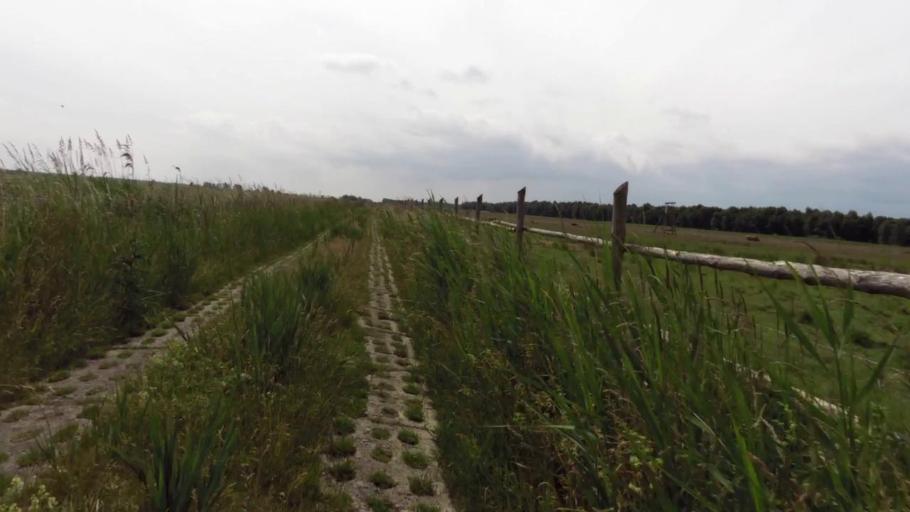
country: PL
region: West Pomeranian Voivodeship
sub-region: Powiat goleniowski
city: Stepnica
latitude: 53.7263
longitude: 14.6050
